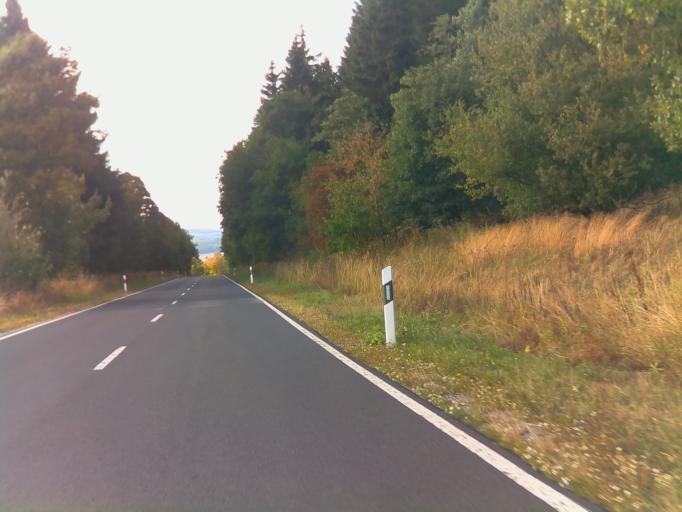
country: DE
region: Thuringia
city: Birx
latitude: 50.5102
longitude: 10.0408
